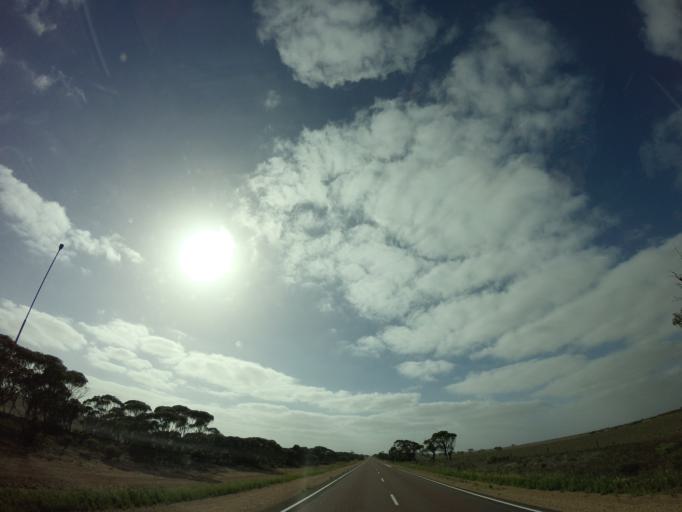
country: AU
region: South Australia
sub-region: Streaky Bay
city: Streaky Bay
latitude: -32.2917
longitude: 134.2371
